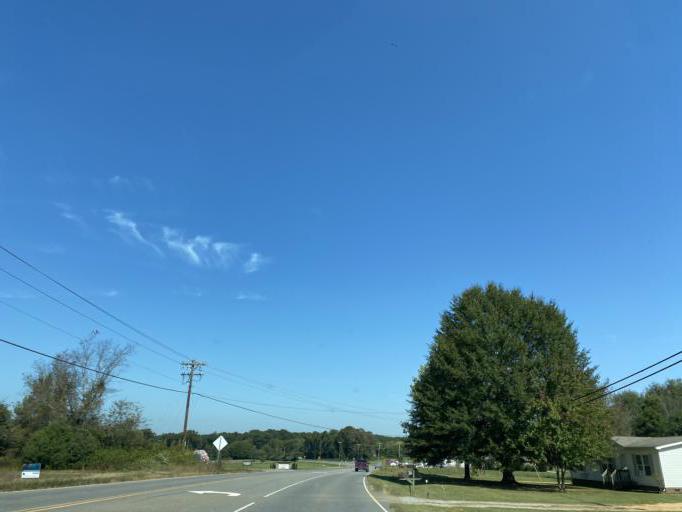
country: US
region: North Carolina
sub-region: Cleveland County
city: Boiling Springs
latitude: 35.2745
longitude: -81.6659
